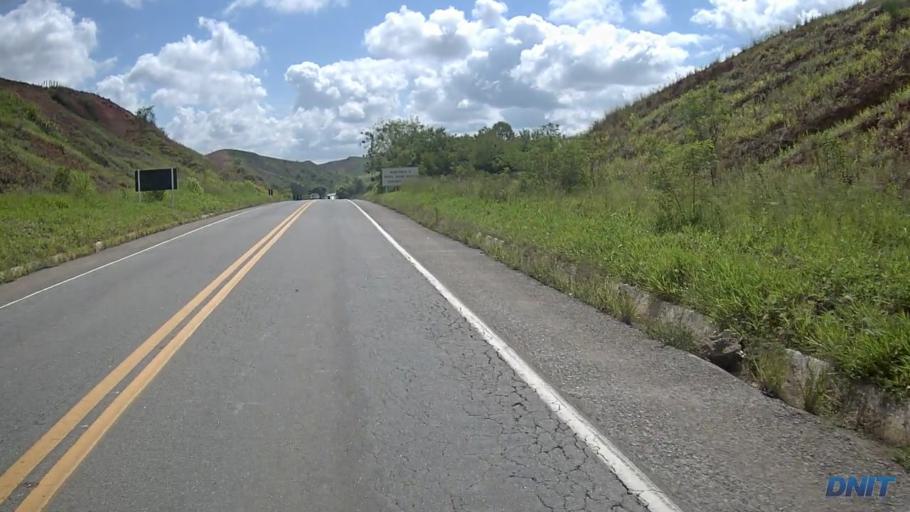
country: BR
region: Minas Gerais
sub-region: Belo Oriente
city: Belo Oriente
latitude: -19.1450
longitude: -42.2291
